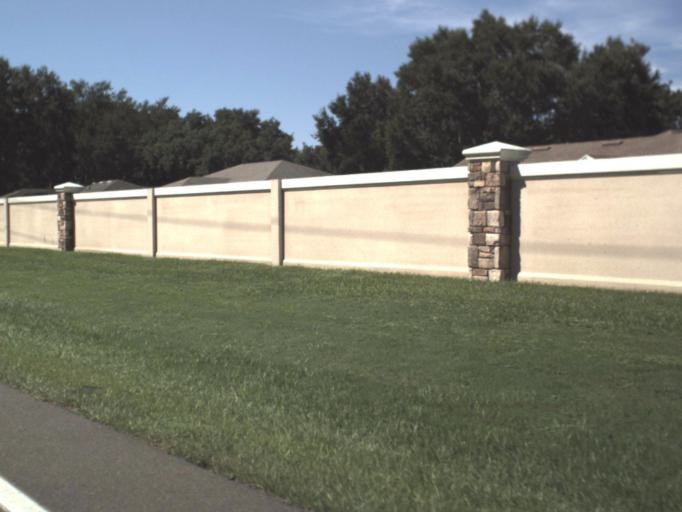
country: US
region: Florida
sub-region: Polk County
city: Auburndale
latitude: 28.1191
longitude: -81.7893
